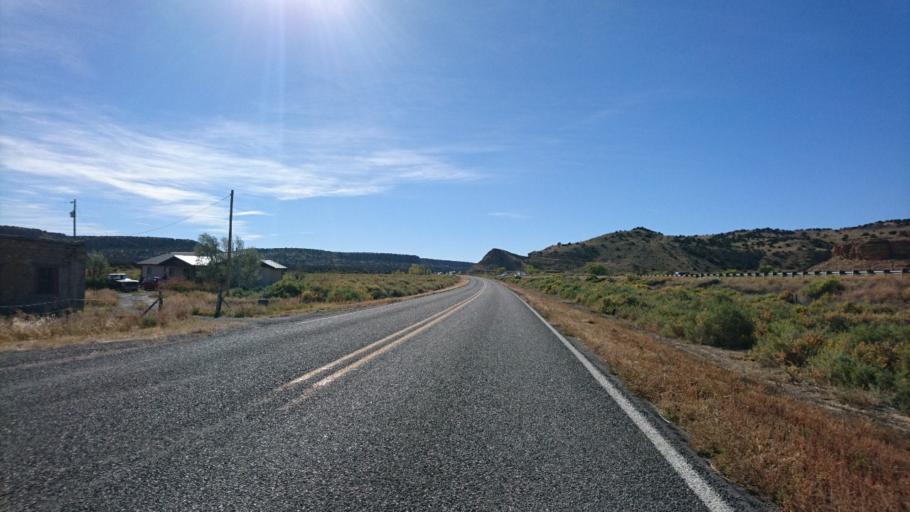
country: US
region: New Mexico
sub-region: Cibola County
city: Skyline-Ganipa
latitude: 35.0692
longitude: -107.6793
